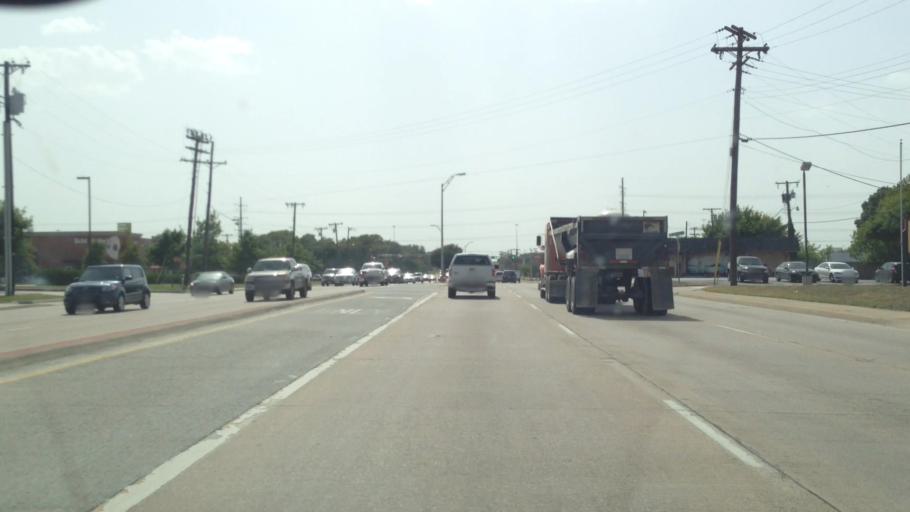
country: US
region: Texas
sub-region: Collin County
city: McKinney
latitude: 33.2163
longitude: -96.6265
